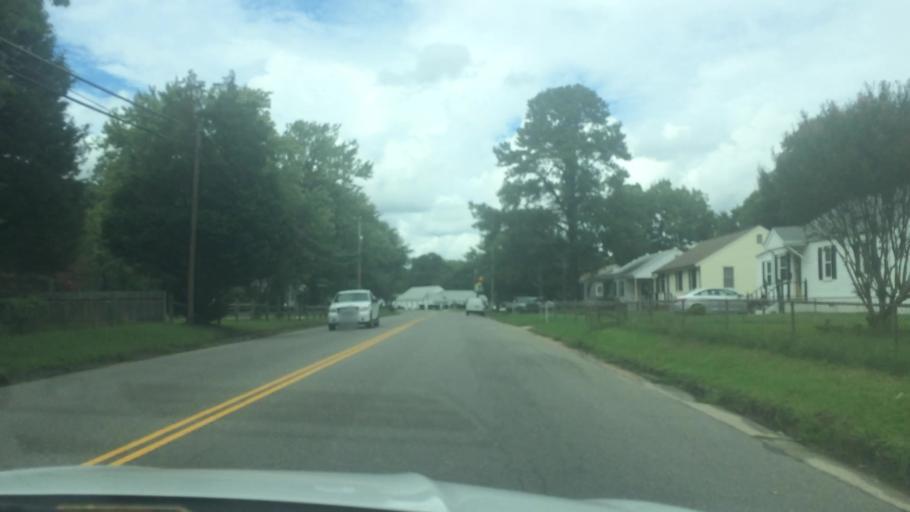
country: US
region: Virginia
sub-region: City of Williamsburg
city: Williamsburg
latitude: 37.2625
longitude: -76.6649
